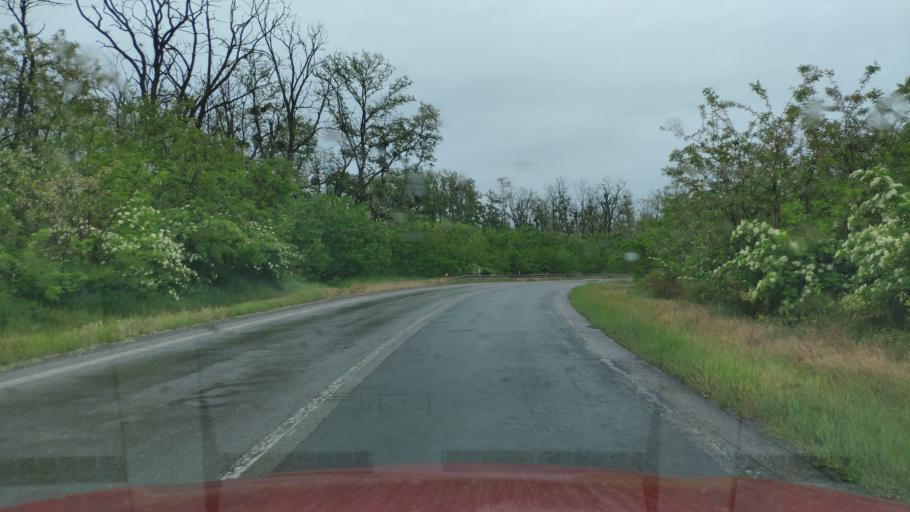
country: HU
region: Borsod-Abauj-Zemplen
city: Ricse
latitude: 48.4416
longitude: 21.9427
